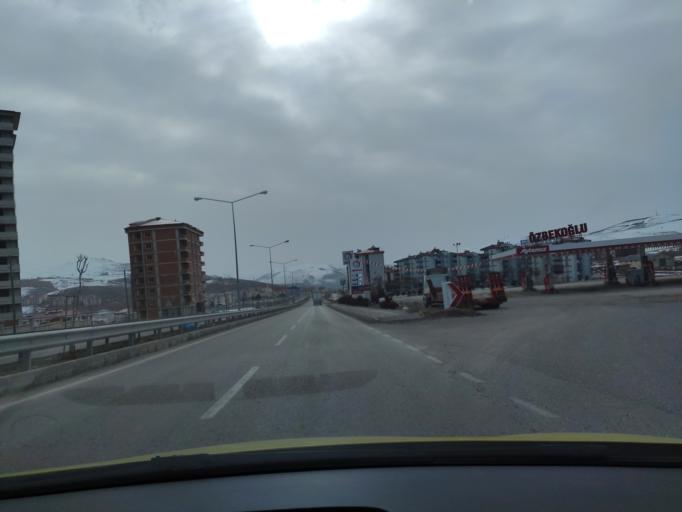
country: TR
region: Bayburt
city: Bayburt
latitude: 40.2695
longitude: 40.1973
